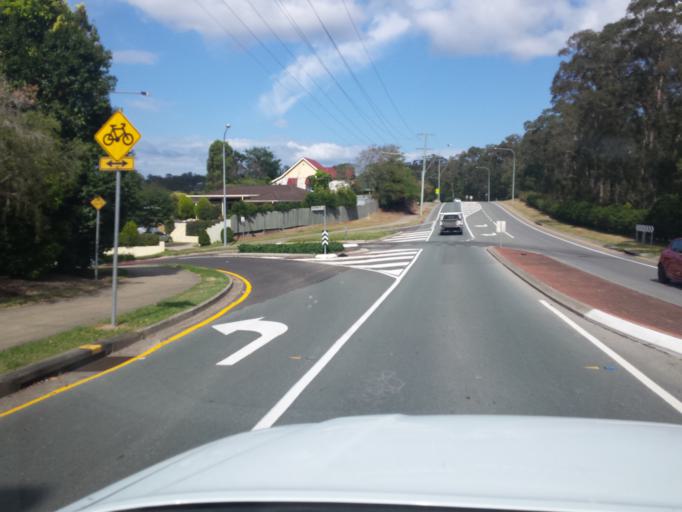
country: AU
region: Queensland
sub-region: Moreton Bay
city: Ferny Hills
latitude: -27.3818
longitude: 152.9457
